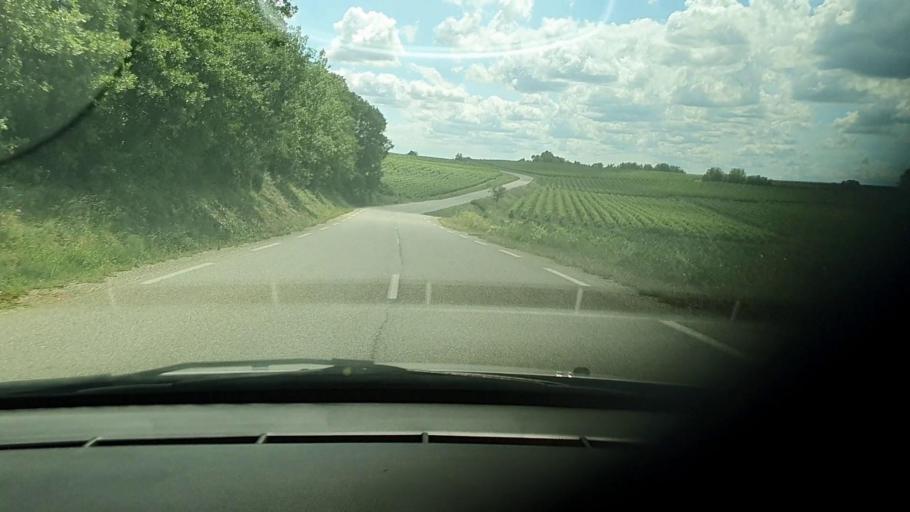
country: FR
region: Languedoc-Roussillon
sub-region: Departement du Gard
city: Moussac
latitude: 44.0203
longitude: 4.2328
